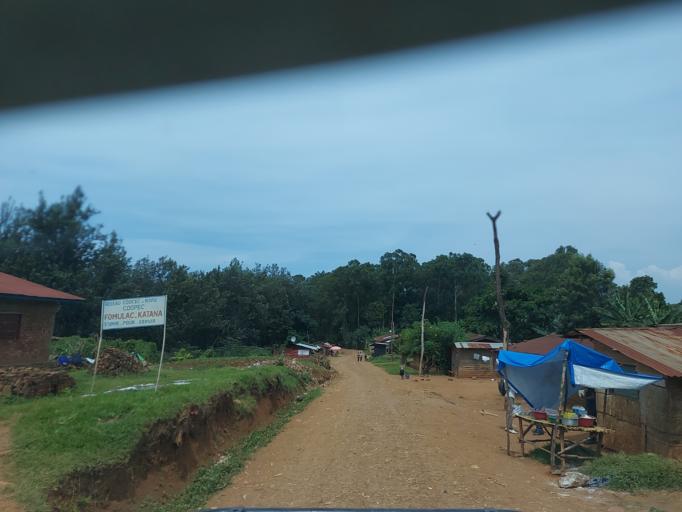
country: RW
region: Western Province
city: Cyangugu
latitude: -2.2351
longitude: 28.8562
